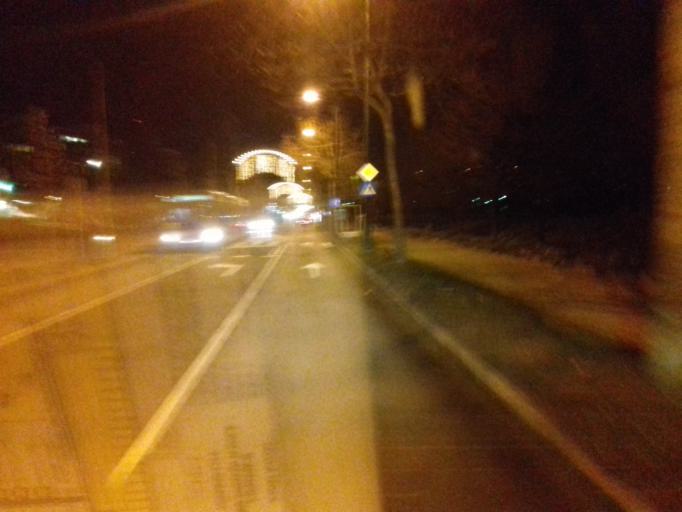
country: BA
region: Federation of Bosnia and Herzegovina
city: Kobilja Glava
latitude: 43.8650
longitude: 18.4108
